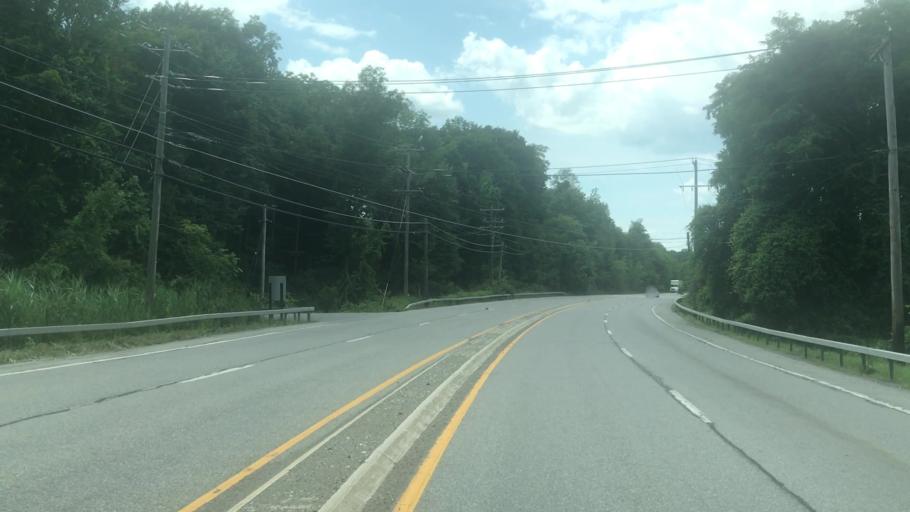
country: US
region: New York
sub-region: Putnam County
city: Peach Lake
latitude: 41.3849
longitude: -73.5769
